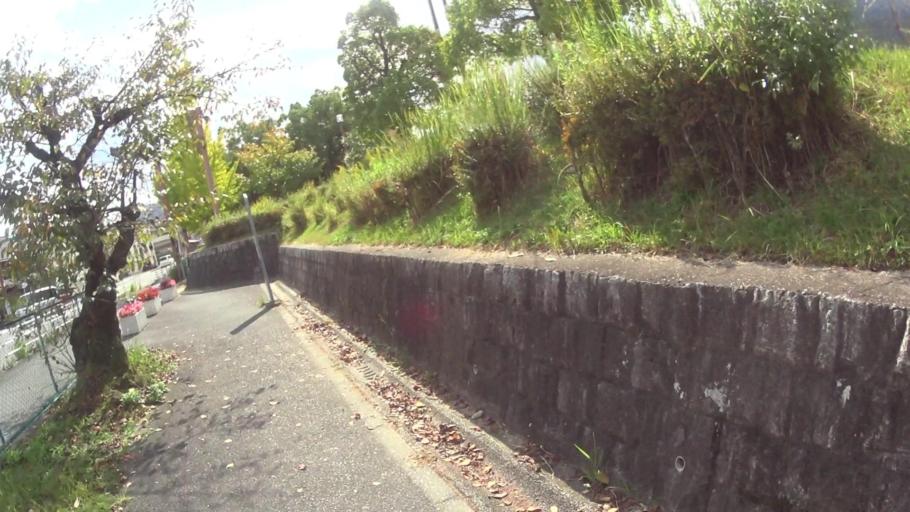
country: JP
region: Shiga Prefecture
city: Otsu-shi
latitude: 35.0200
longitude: 135.8583
